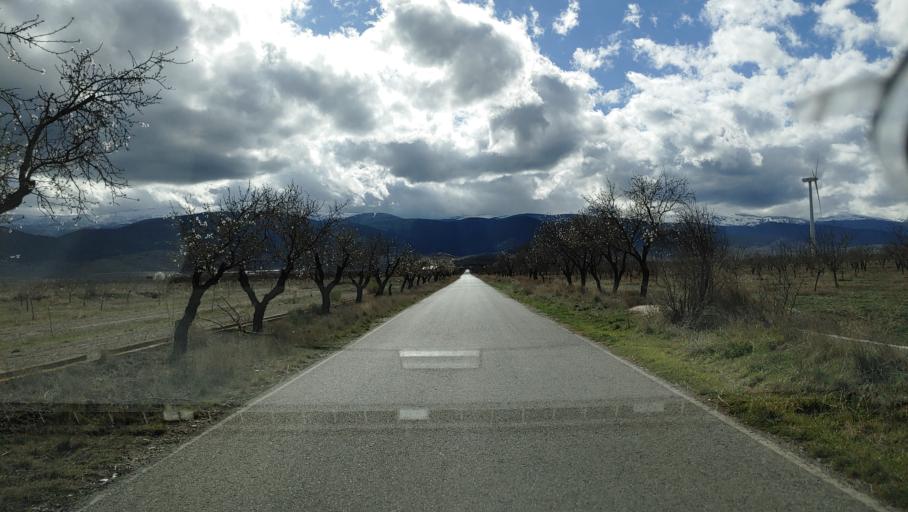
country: ES
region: Andalusia
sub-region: Provincia de Granada
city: Hueneja
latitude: 37.2052
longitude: -2.9779
